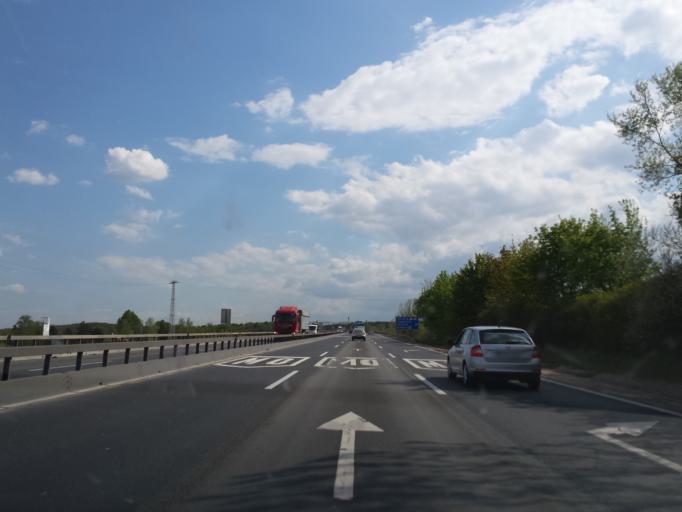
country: HU
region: Pest
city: Toeroekbalint
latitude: 47.4404
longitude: 18.8913
